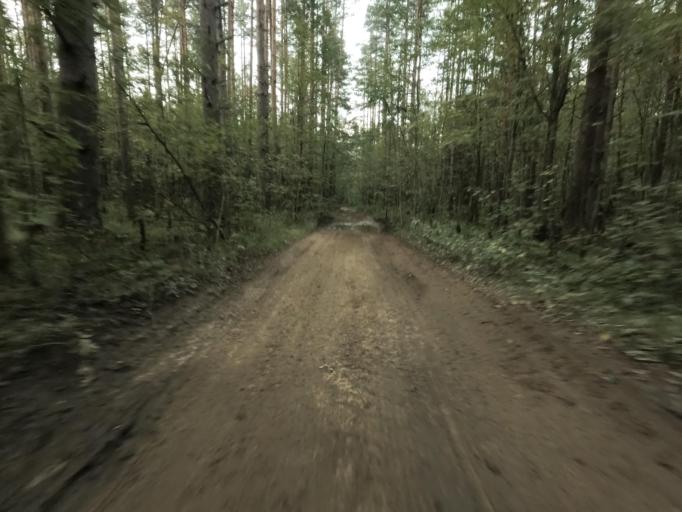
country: RU
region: Leningrad
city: Otradnoye
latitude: 59.8504
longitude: 30.7959
